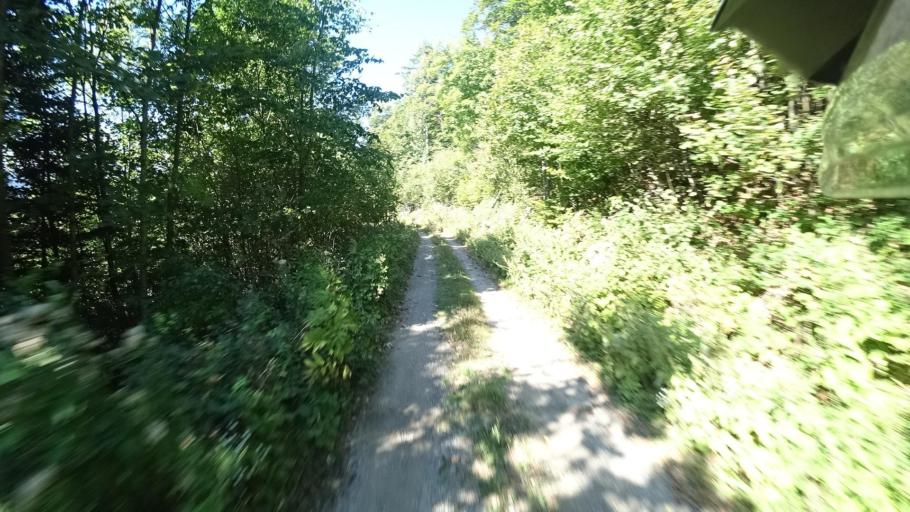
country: HR
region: Karlovacka
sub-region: Grad Ogulin
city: Ogulin
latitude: 45.2616
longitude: 15.1346
